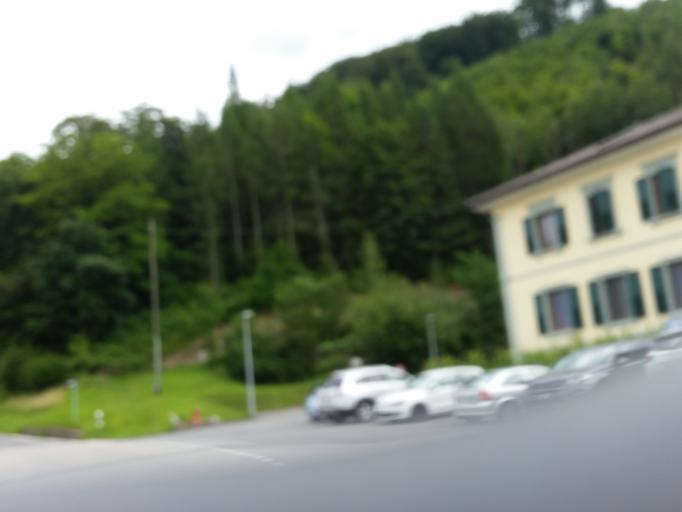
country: CH
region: Vaud
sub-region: Broye-Vully District
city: Moudon
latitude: 46.6669
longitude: 6.8062
